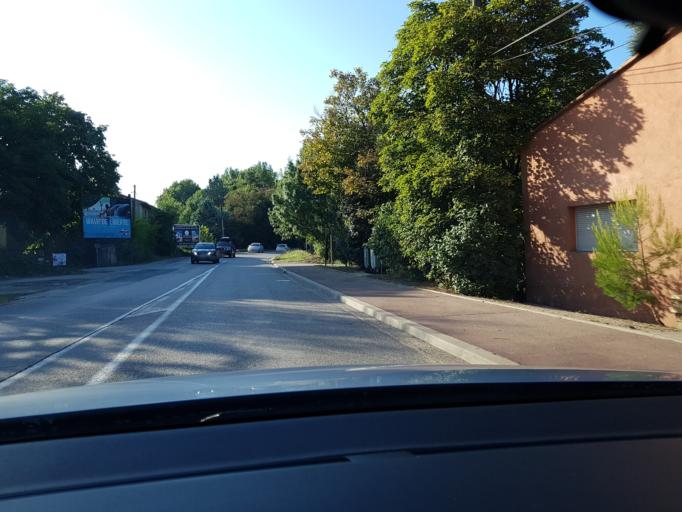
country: FR
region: Provence-Alpes-Cote d'Azur
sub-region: Departement des Bouches-du-Rhone
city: Chateauneuf-le-Rouge
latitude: 43.4814
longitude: 5.5343
